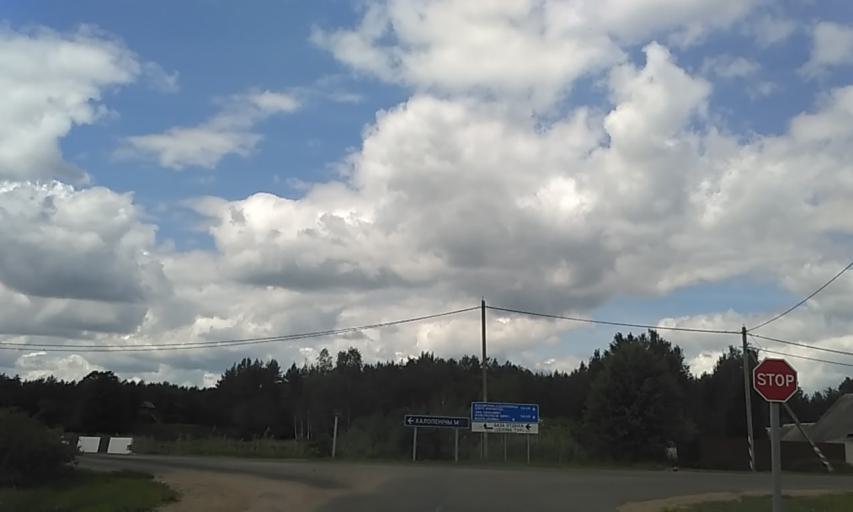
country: BY
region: Minsk
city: Krupki
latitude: 54.4861
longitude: 29.1527
